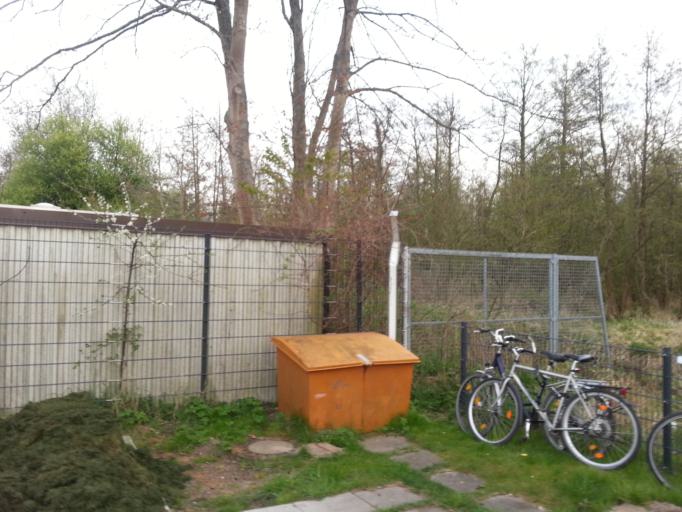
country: DE
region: Schleswig-Holstein
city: Timmendorfer Strand
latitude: 53.9941
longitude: 10.7838
